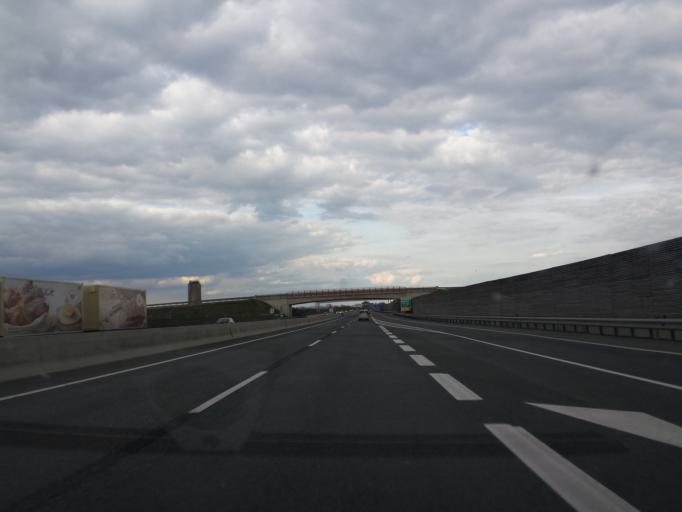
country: AT
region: Lower Austria
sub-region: Politischer Bezirk Krems
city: Grafenegg
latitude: 48.4091
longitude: 15.7510
